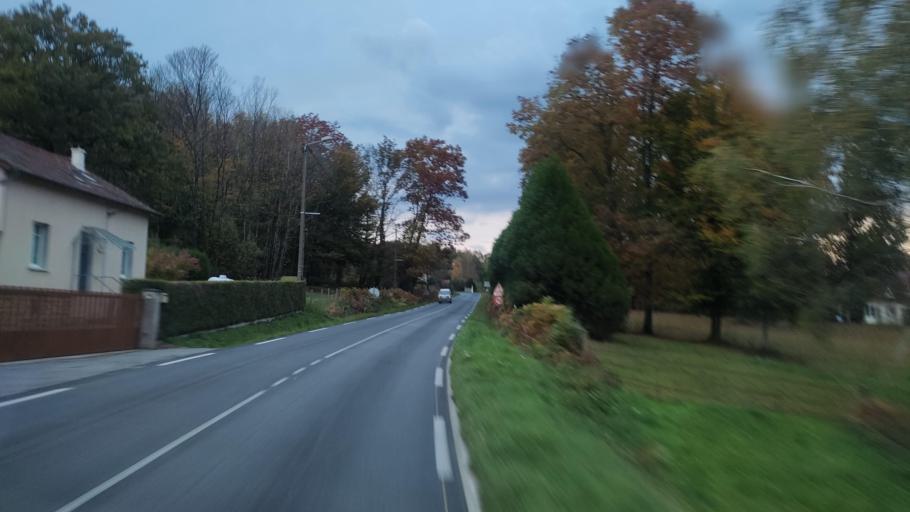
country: FR
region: Limousin
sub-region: Departement de la Haute-Vienne
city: Ambazac
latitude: 45.9903
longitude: 1.4430
